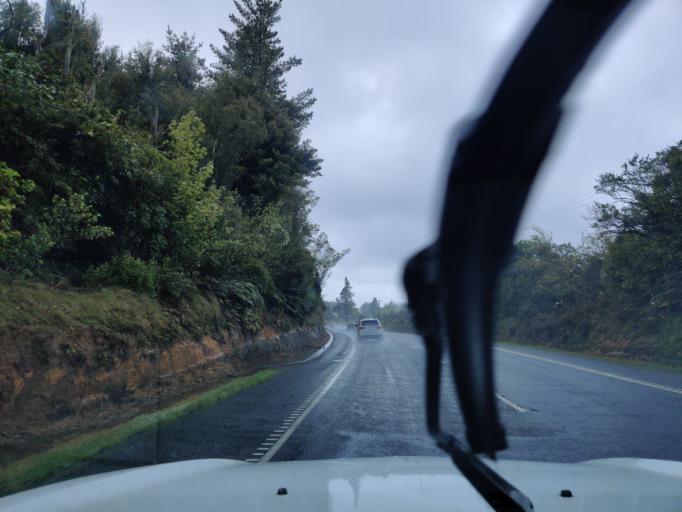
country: NZ
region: Bay of Plenty
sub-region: Rotorua District
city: Rotorua
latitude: -38.0598
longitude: 176.0931
